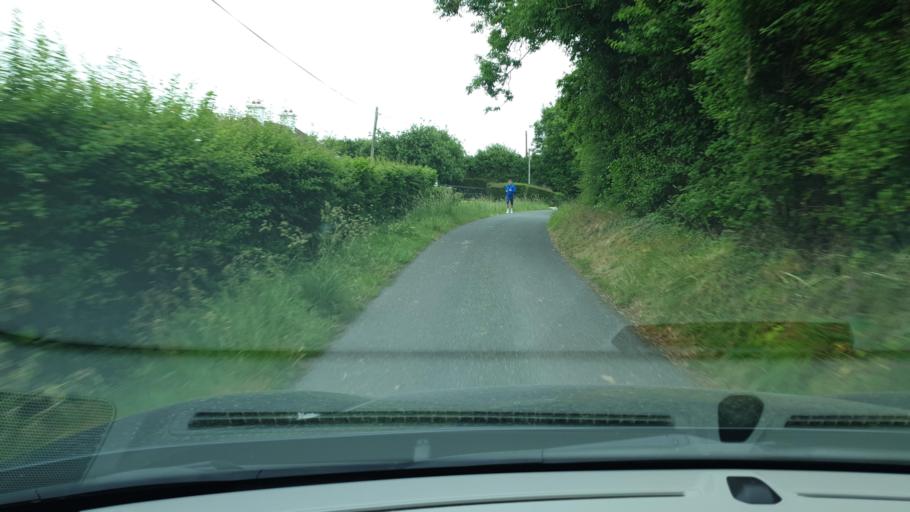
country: IE
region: Leinster
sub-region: An Mhi
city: Ashbourne
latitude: 53.4801
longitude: -6.3961
